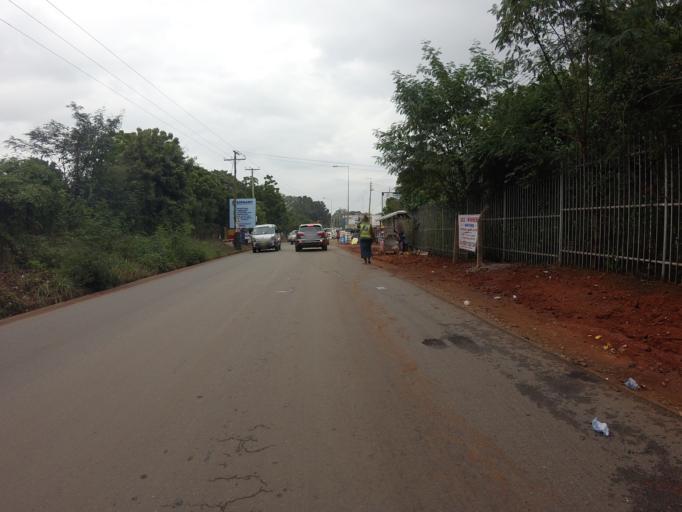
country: GH
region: Greater Accra
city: Dome
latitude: 5.6313
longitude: -0.2186
